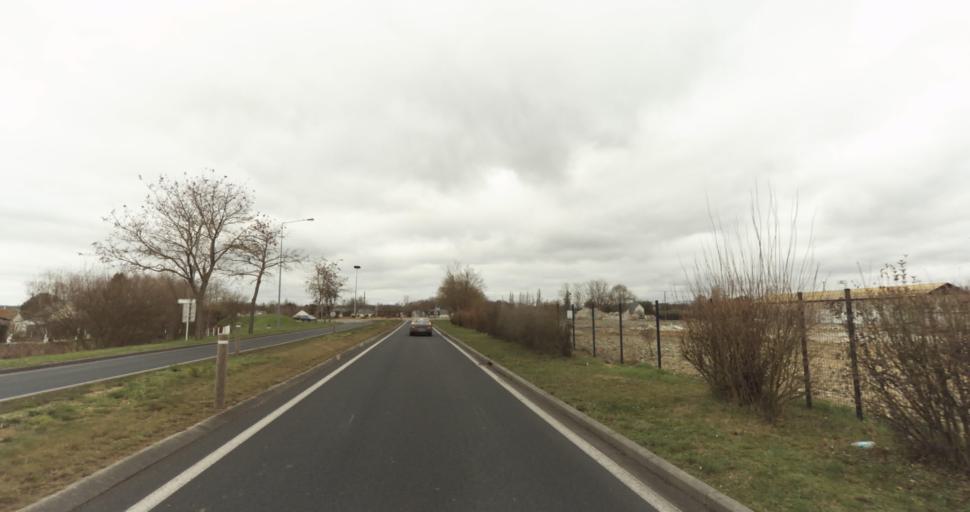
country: FR
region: Pays de la Loire
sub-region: Departement de Maine-et-Loire
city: Jumelles
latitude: 47.3878
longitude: -0.1152
